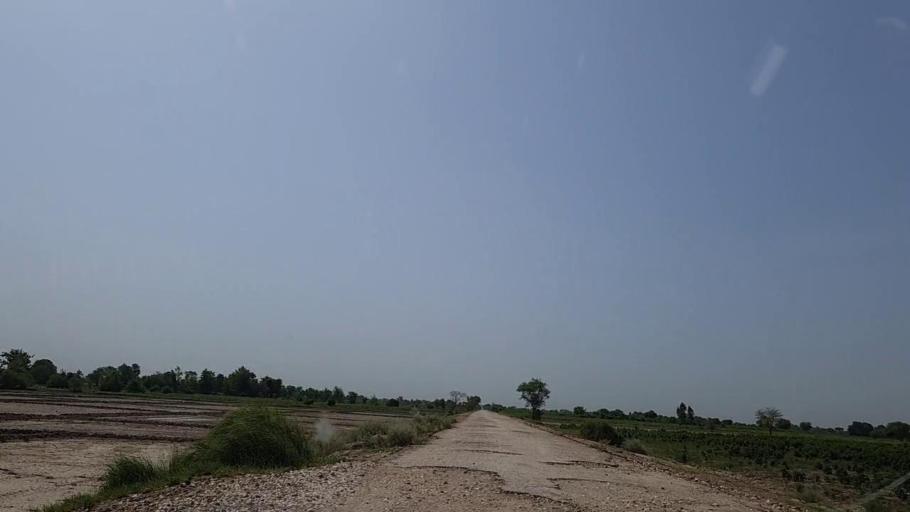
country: PK
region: Sindh
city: Naushahro Firoz
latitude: 26.8577
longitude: 68.0064
